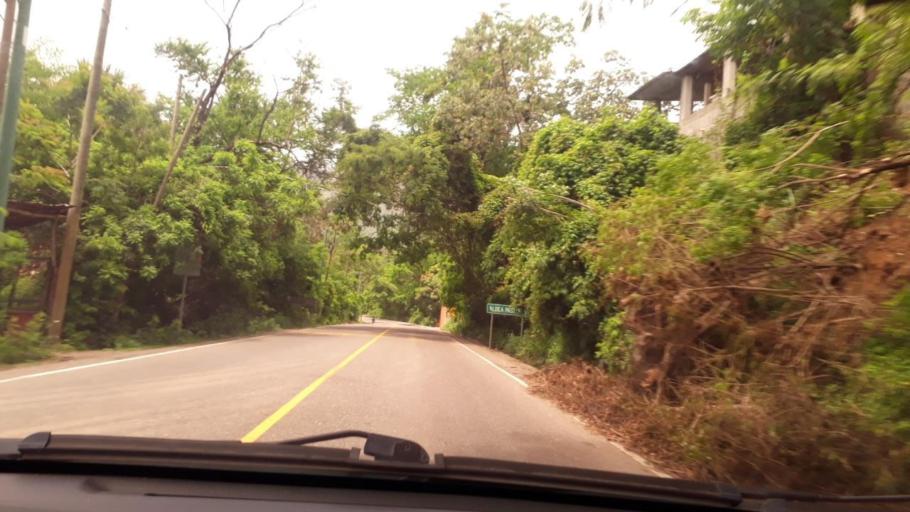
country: GT
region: Chiquimula
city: San Jacinto
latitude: 14.7011
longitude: -89.4993
